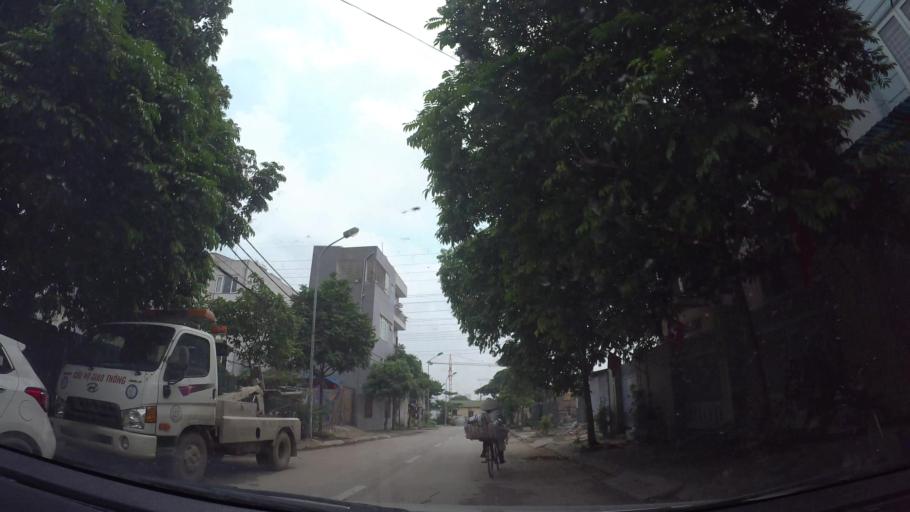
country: VN
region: Ha Noi
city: Tay Ho
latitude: 21.0870
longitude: 105.7956
